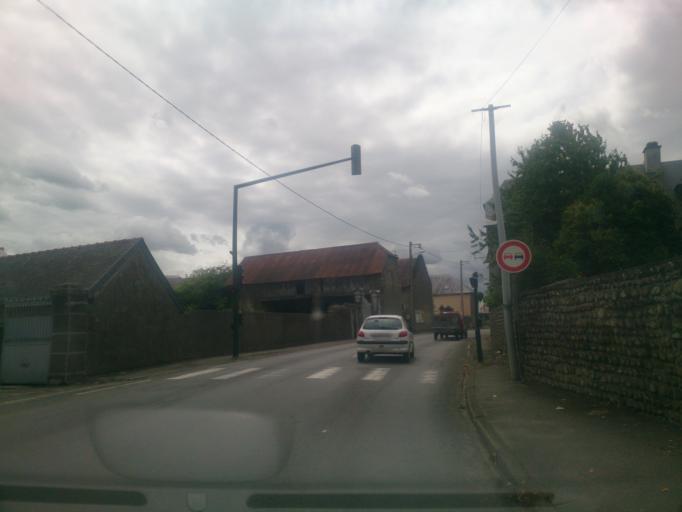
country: FR
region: Midi-Pyrenees
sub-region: Departement des Hautes-Pyrenees
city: Horgues
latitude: 43.1880
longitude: 0.0887
